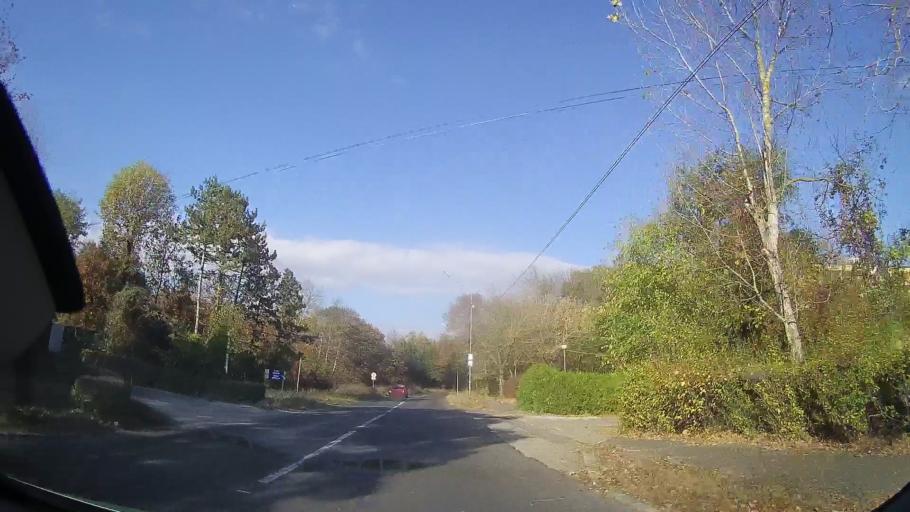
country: RO
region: Constanta
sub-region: Comuna Douazeci si Trei August
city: Douazeci si Trei August
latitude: 43.8693
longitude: 28.5948
